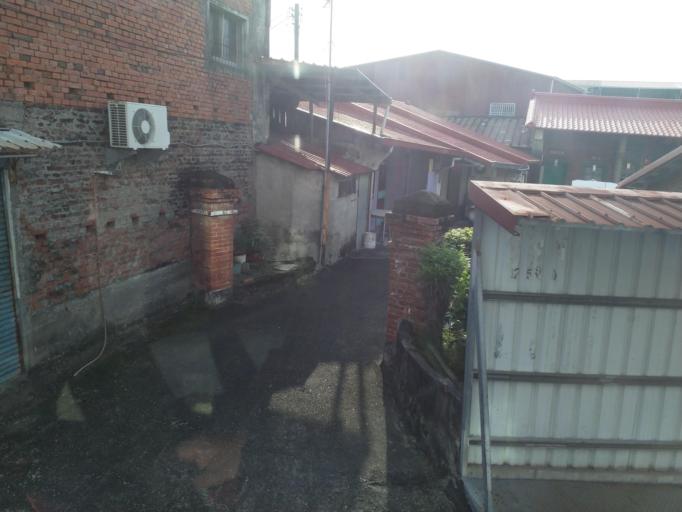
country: TW
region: Taiwan
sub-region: Pingtung
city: Pingtung
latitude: 22.8977
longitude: 120.5429
